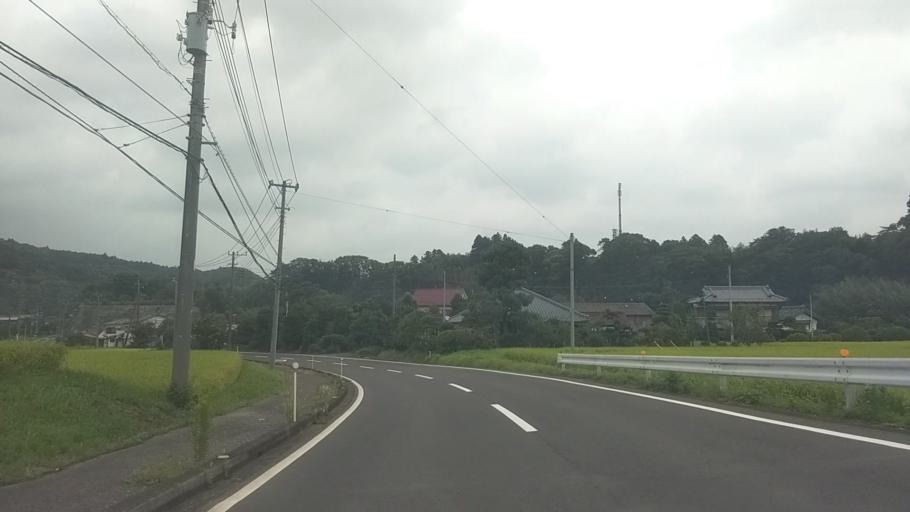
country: JP
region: Chiba
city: Kawaguchi
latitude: 35.2539
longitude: 140.0428
